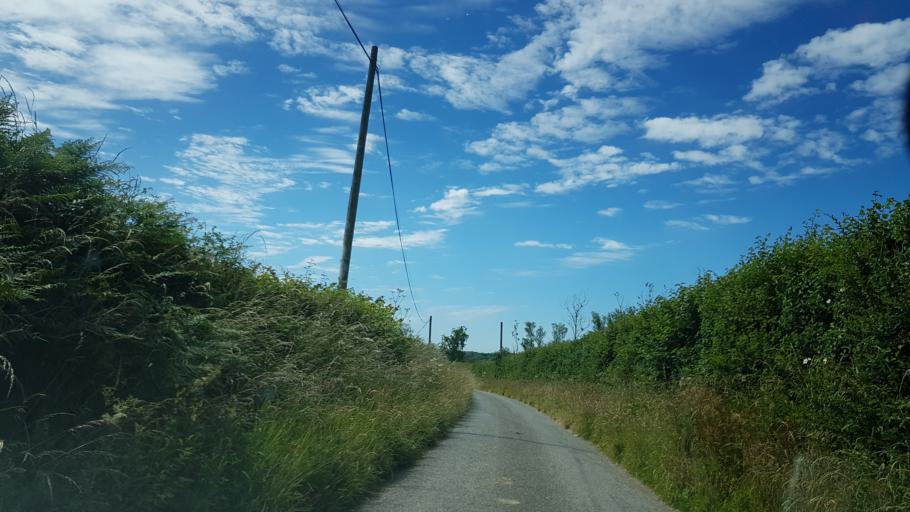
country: GB
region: Wales
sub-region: Pembrokeshire
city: Haverfordwest
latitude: 51.8216
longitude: -4.9230
